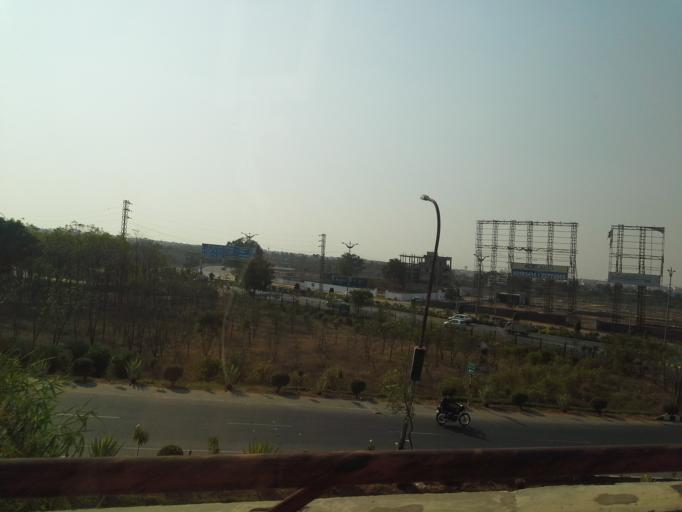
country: IN
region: Telangana
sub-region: Rangareddi
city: Sriramnagar
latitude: 17.2545
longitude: 78.3817
